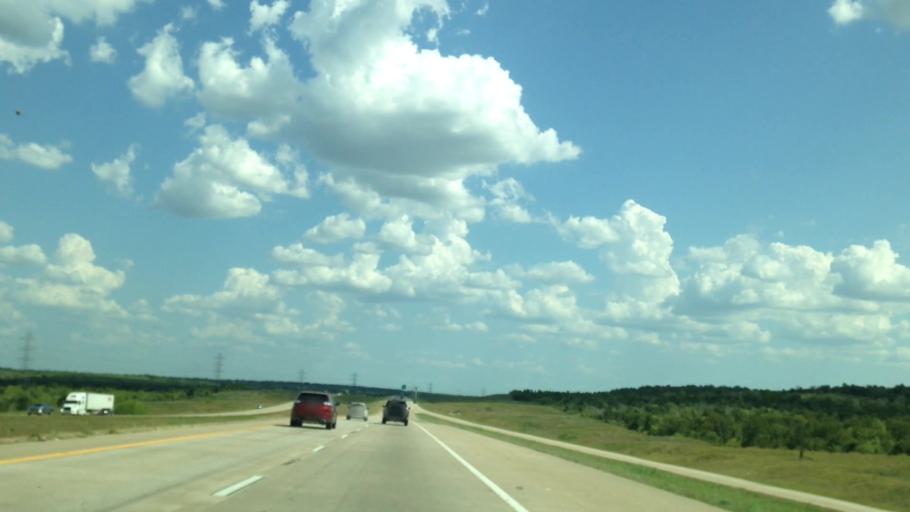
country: US
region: Texas
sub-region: Travis County
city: Manor
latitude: 30.3218
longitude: -97.5793
